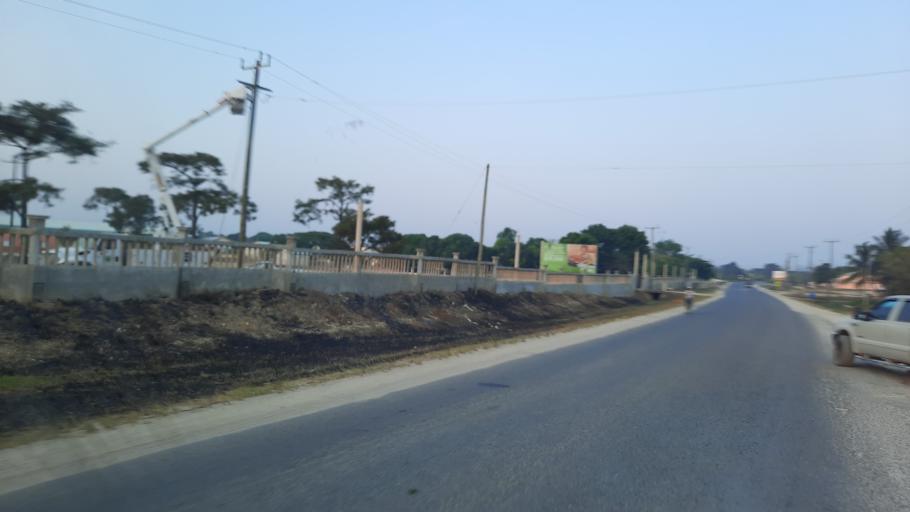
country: BZ
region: Stann Creek
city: Placencia
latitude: 16.5350
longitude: -88.4257
